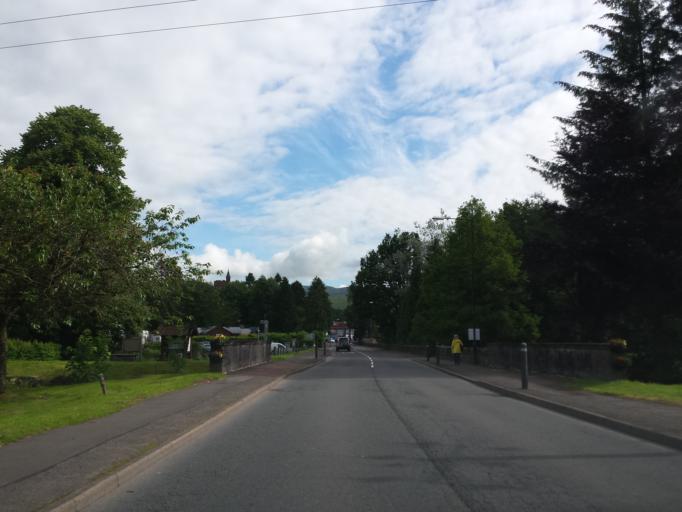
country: GB
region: Scotland
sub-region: Dumfries and Galloway
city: Moffat
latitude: 55.3289
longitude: -3.4462
